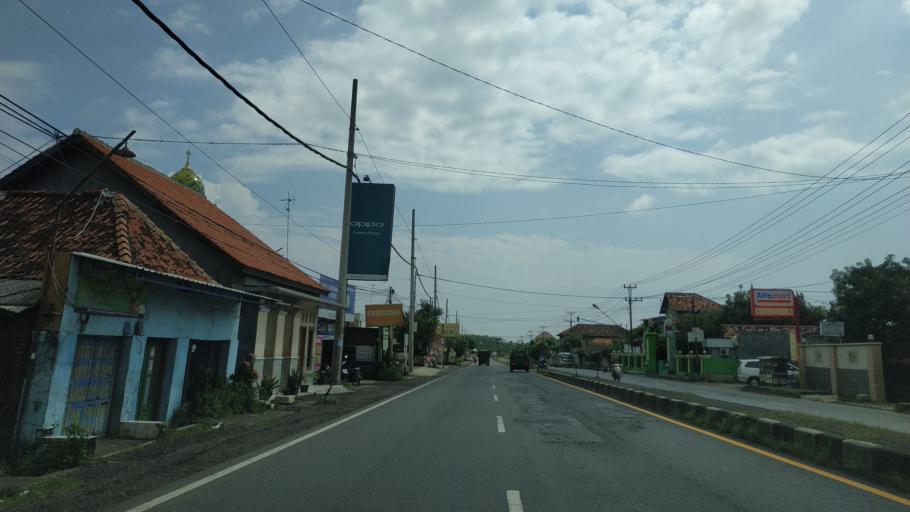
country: ID
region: Central Java
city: Pekalongan
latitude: -6.9499
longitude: 109.8084
